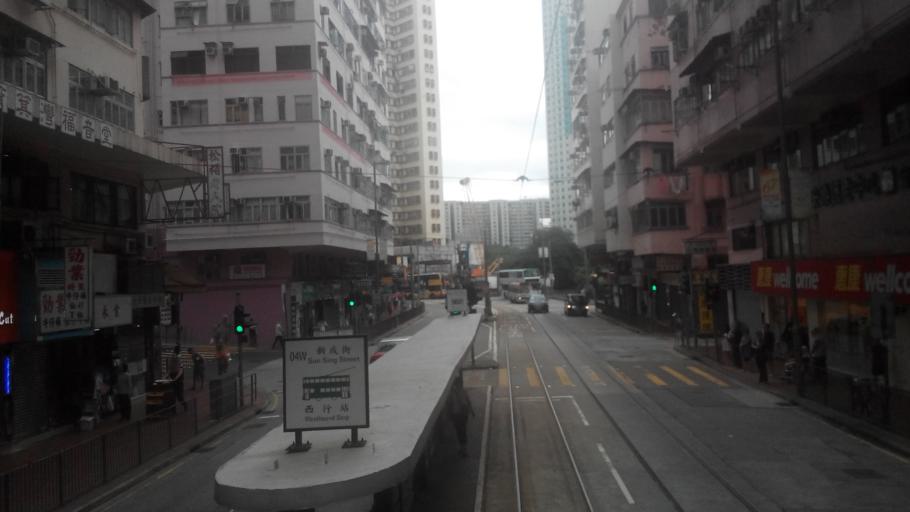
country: HK
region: Wanchai
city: Wan Chai
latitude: 22.2795
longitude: 114.2258
